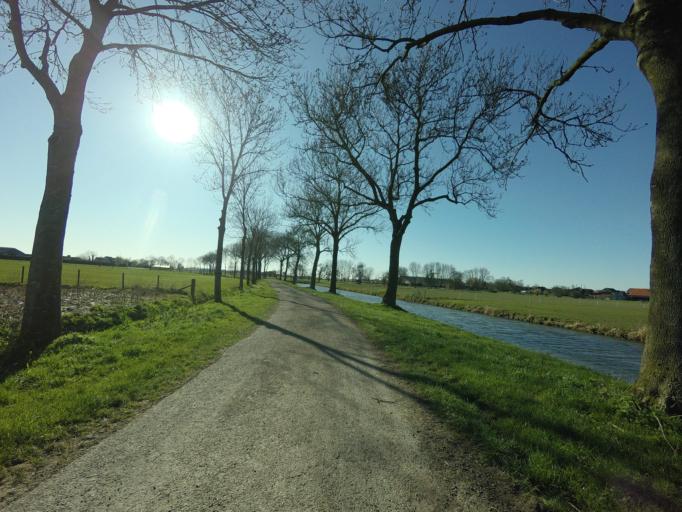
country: NL
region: Utrecht
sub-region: Gemeente Utrechtse Heuvelrug
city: Leersum
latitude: 51.9552
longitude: 5.4096
